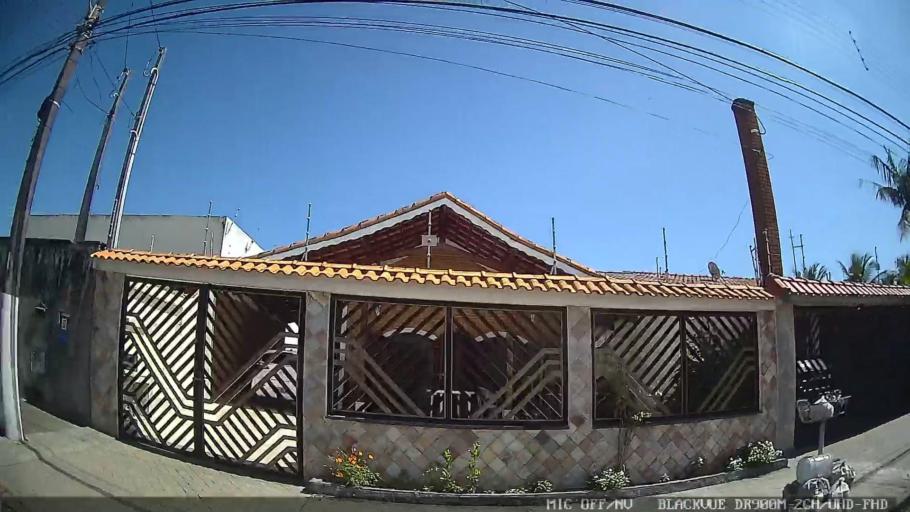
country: BR
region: Sao Paulo
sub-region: Peruibe
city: Peruibe
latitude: -24.2950
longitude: -46.9693
